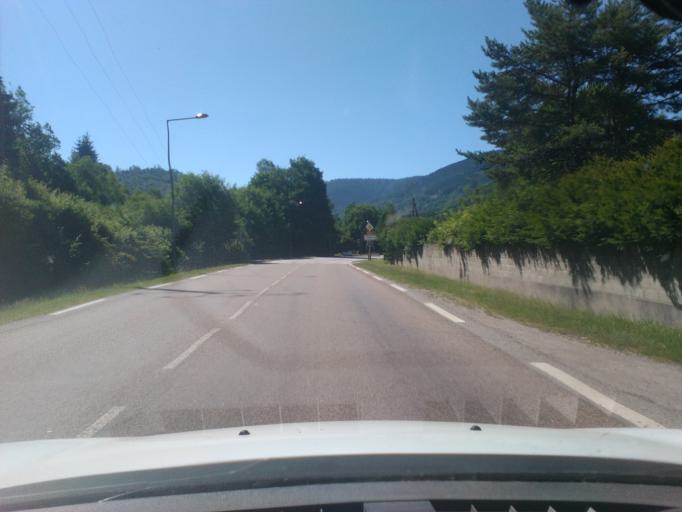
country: FR
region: Lorraine
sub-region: Departement des Vosges
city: Vagney
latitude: 47.9754
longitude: 6.7278
